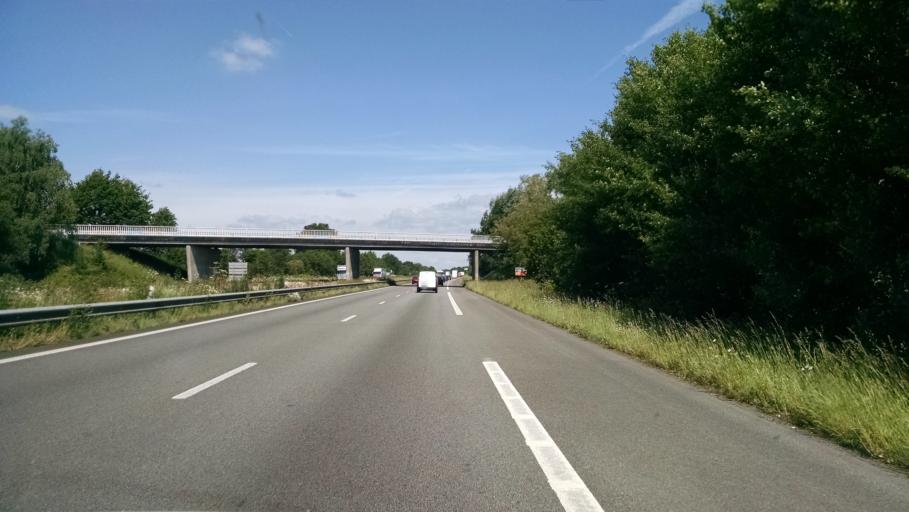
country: FR
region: Pays de la Loire
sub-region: Departement de la Loire-Atlantique
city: Sautron
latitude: 47.2689
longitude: -1.7130
